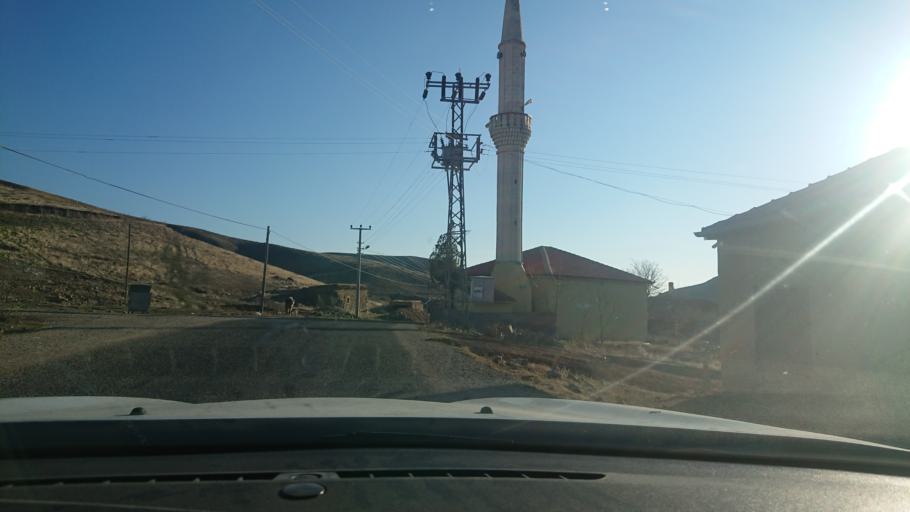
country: TR
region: Aksaray
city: Acipinar
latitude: 38.6926
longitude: 33.7472
